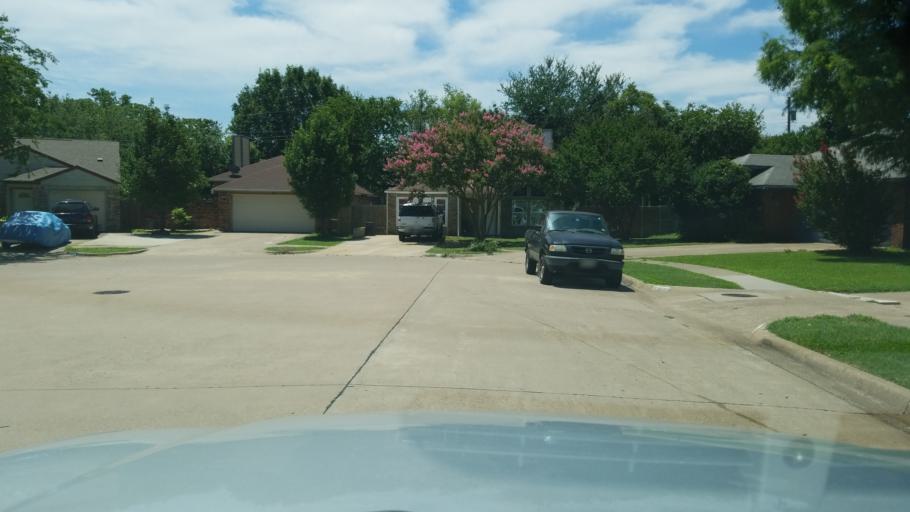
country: US
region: Texas
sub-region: Dallas County
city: Irving
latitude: 32.7996
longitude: -96.9285
